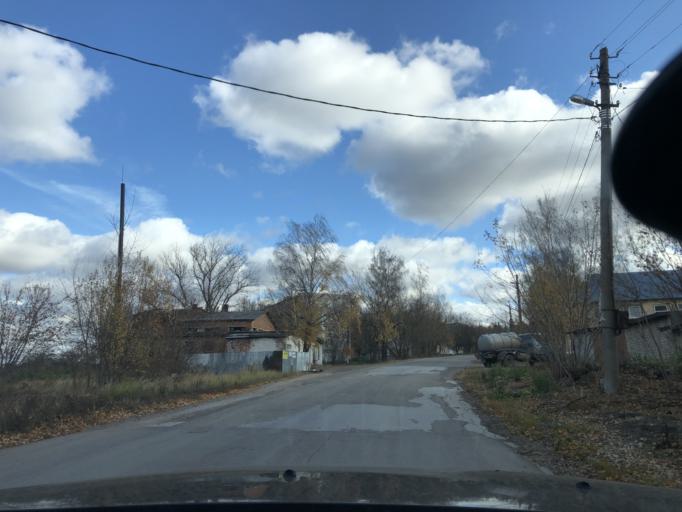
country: RU
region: Tula
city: Gorelki
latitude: 54.2959
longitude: 37.5652
